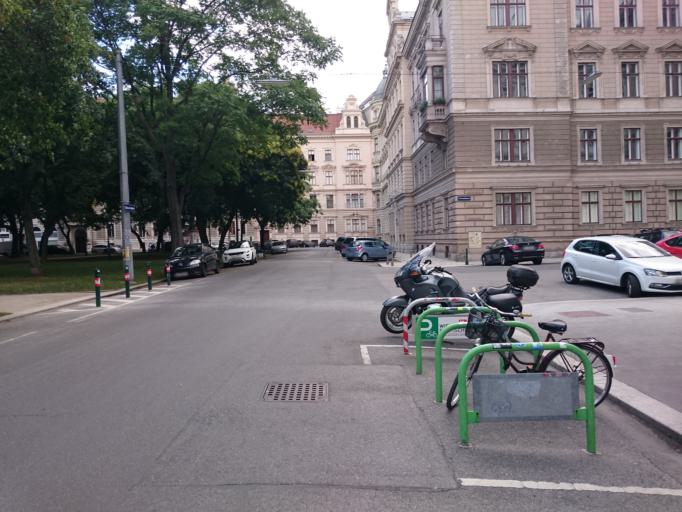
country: AT
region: Vienna
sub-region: Wien Stadt
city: Vienna
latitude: 48.2160
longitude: 16.3583
